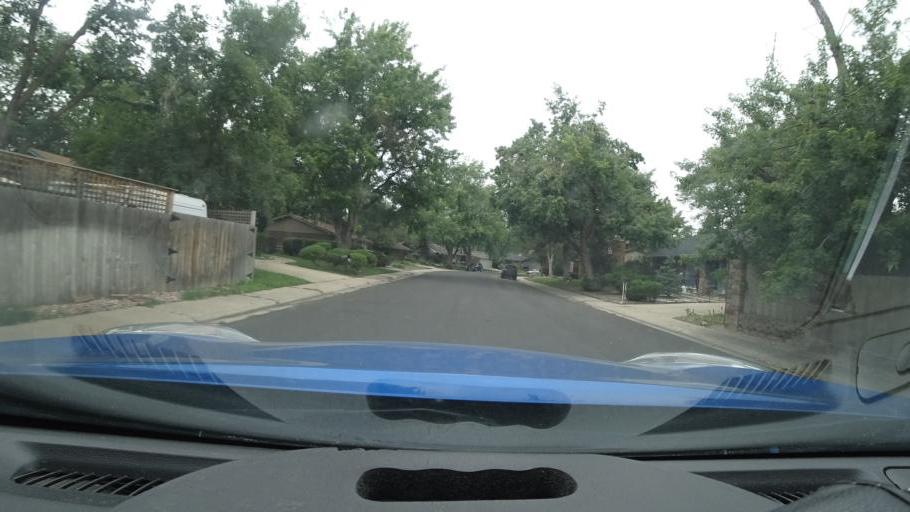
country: US
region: Colorado
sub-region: Arapahoe County
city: Glendale
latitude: 39.6824
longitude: -104.9052
